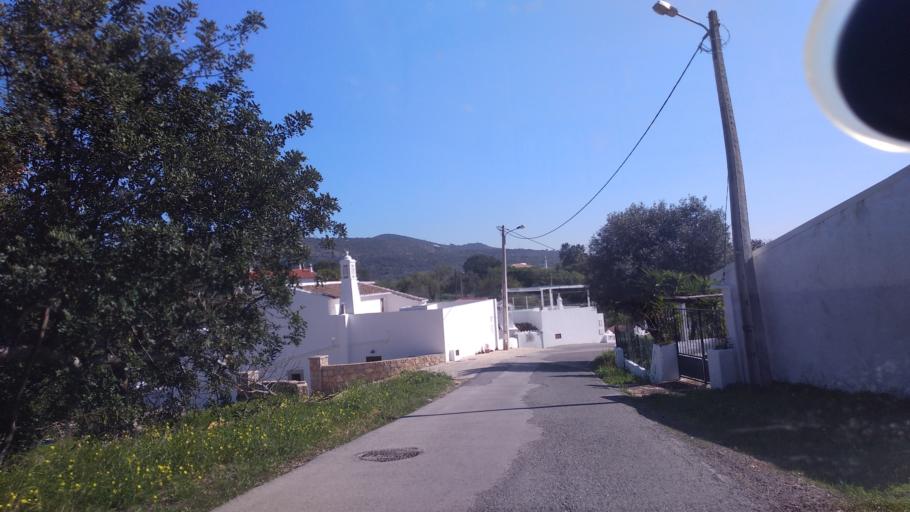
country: PT
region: Faro
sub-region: Faro
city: Santa Barbara de Nexe
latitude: 37.1112
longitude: -7.9173
